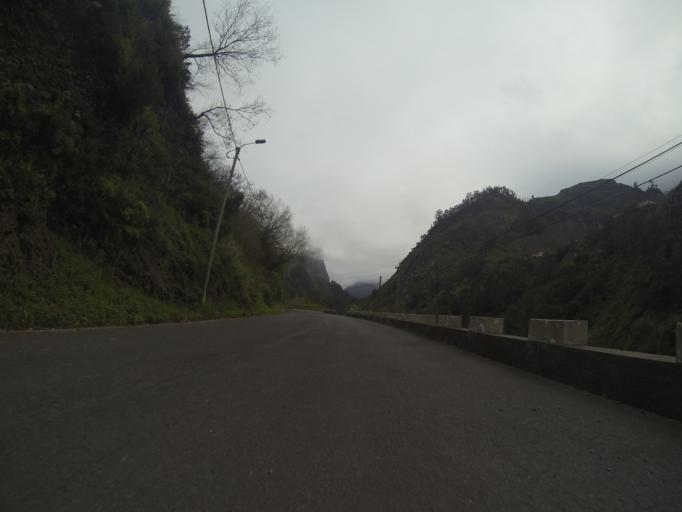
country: PT
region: Madeira
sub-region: Camara de Lobos
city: Curral das Freiras
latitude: 32.7268
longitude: -16.9660
